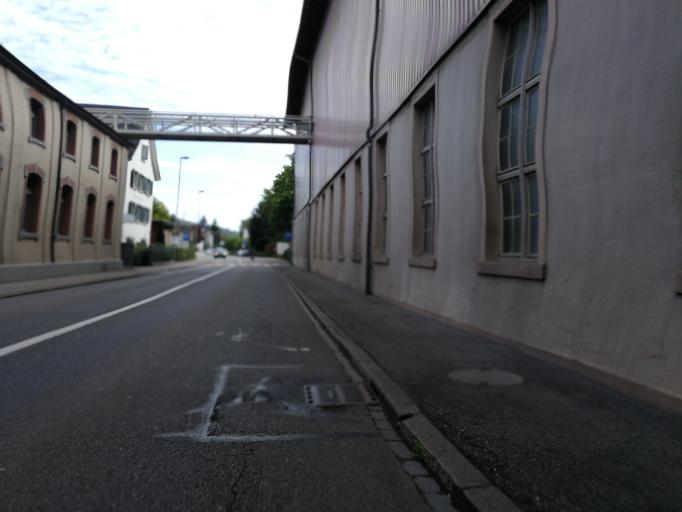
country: CH
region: Zurich
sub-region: Bezirk Meilen
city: Uetikon
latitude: 47.2599
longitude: 8.6740
